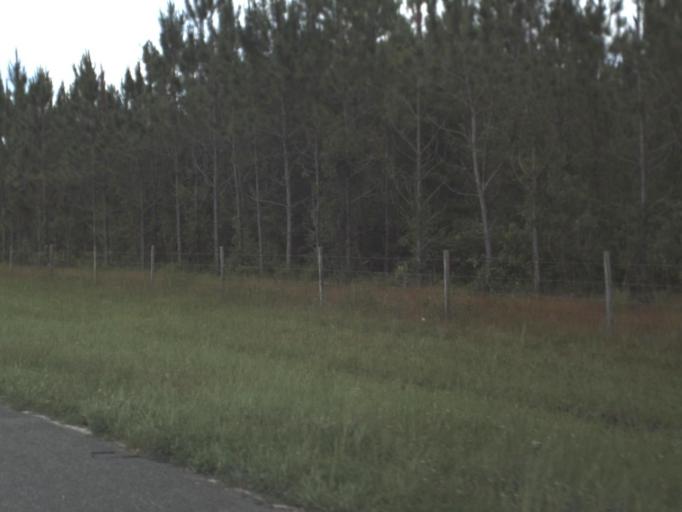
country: US
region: Florida
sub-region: Clay County
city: Middleburg
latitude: 29.9749
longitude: -81.8977
